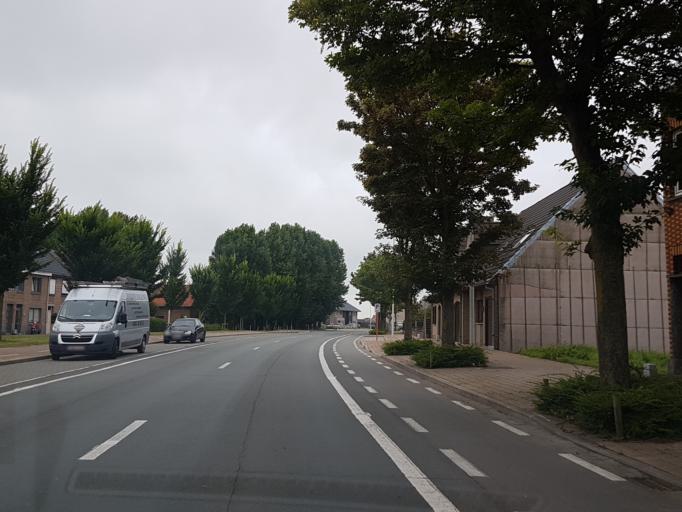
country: BE
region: Flanders
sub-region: Provincie West-Vlaanderen
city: Bredene
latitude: 51.2298
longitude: 2.9667
